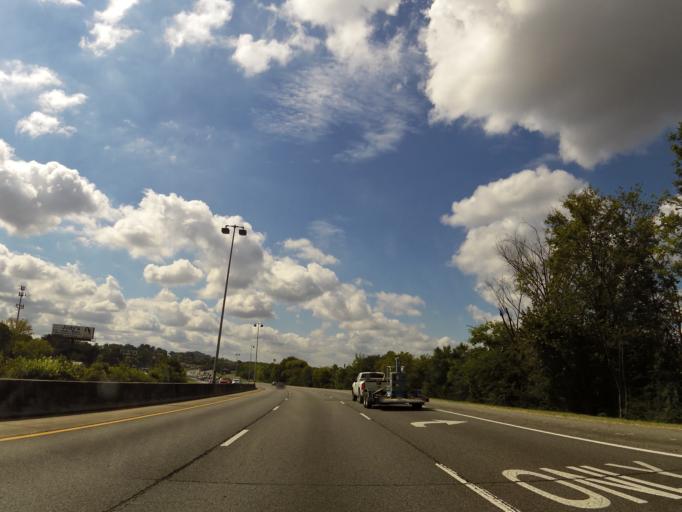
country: US
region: Alabama
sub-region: Jefferson County
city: Fairfield
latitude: 33.4920
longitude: -86.9173
